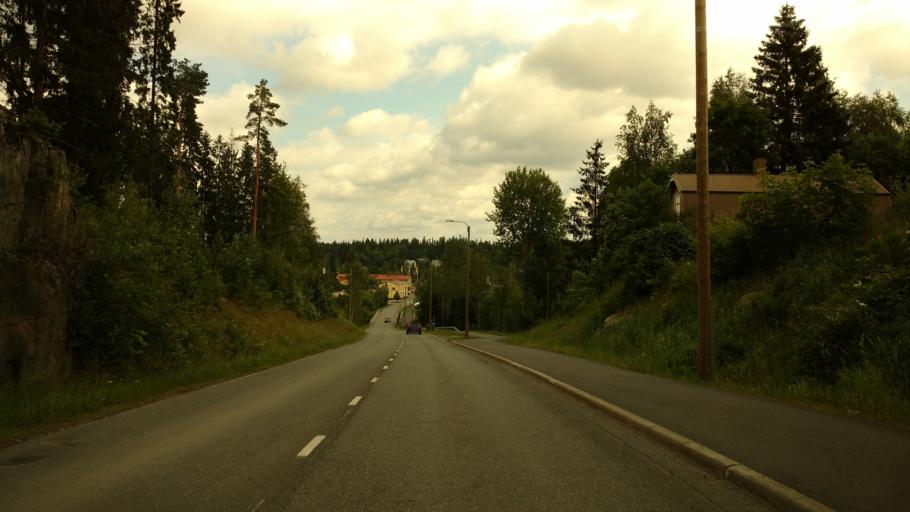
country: FI
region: Haeme
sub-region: Forssa
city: Ypaejae
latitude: 60.7996
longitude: 23.2798
